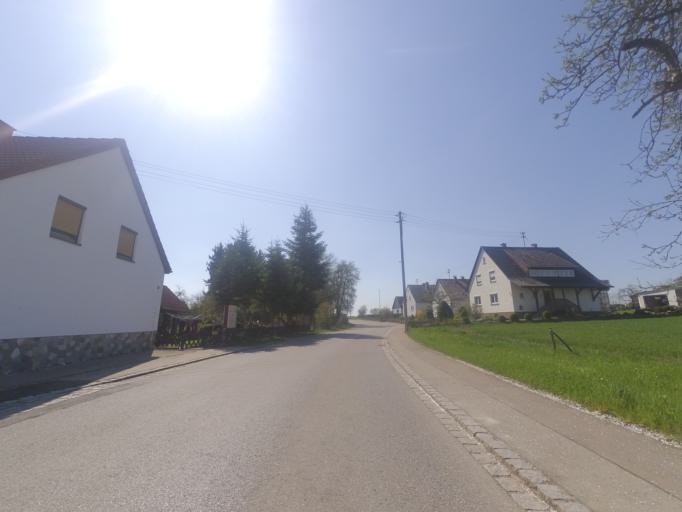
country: DE
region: Bavaria
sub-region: Swabia
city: Pfaffenhofen an der Roth
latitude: 48.3419
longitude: 10.1987
